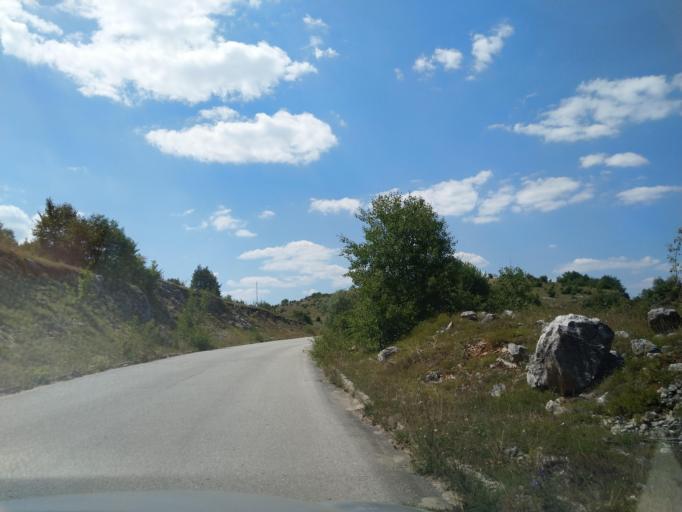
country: RS
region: Central Serbia
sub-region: Zlatiborski Okrug
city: Nova Varos
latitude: 43.4263
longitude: 19.9443
